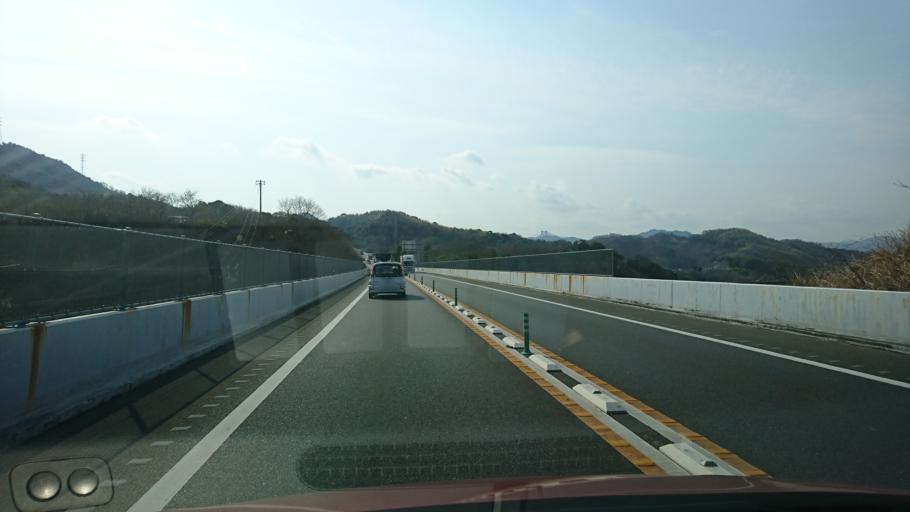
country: JP
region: Hiroshima
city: Onomichi
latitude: 34.3765
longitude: 133.1916
